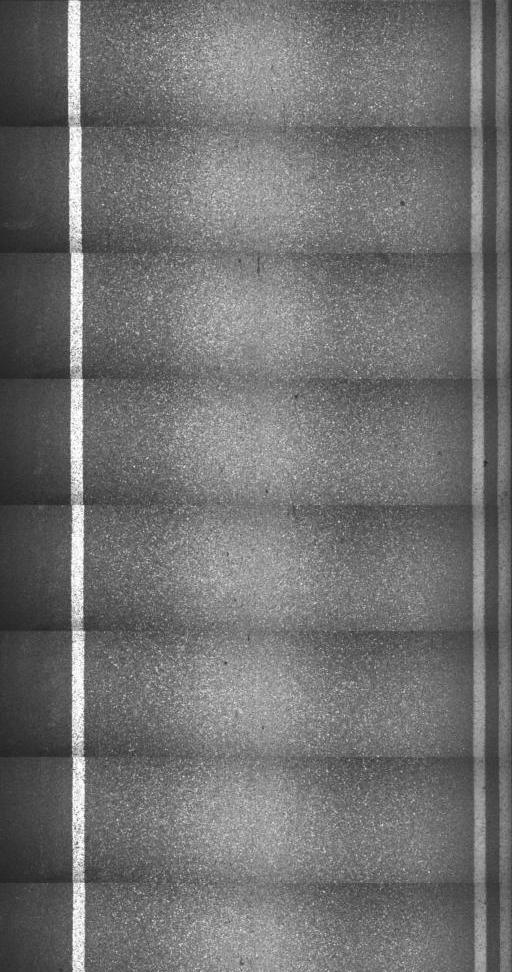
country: US
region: Vermont
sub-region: Chittenden County
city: Colchester
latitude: 44.5597
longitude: -73.1614
